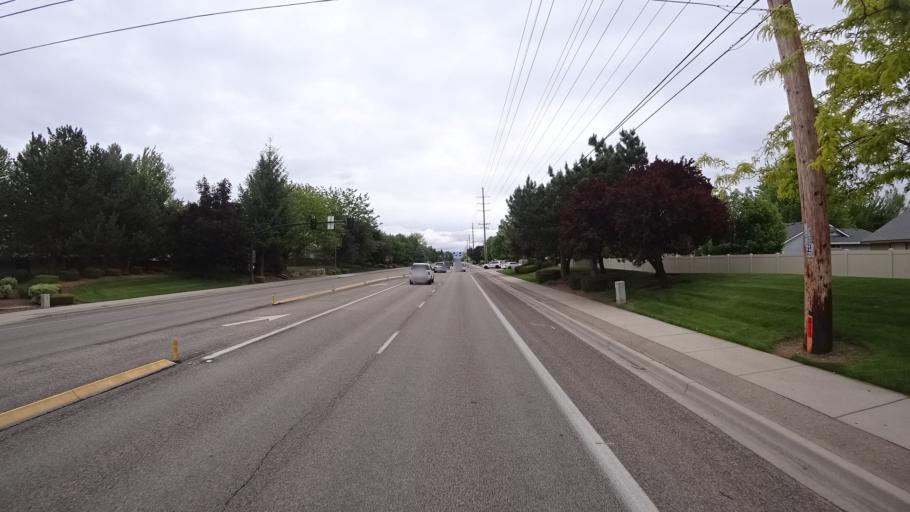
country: US
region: Idaho
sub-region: Ada County
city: Eagle
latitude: 43.6484
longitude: -116.3508
